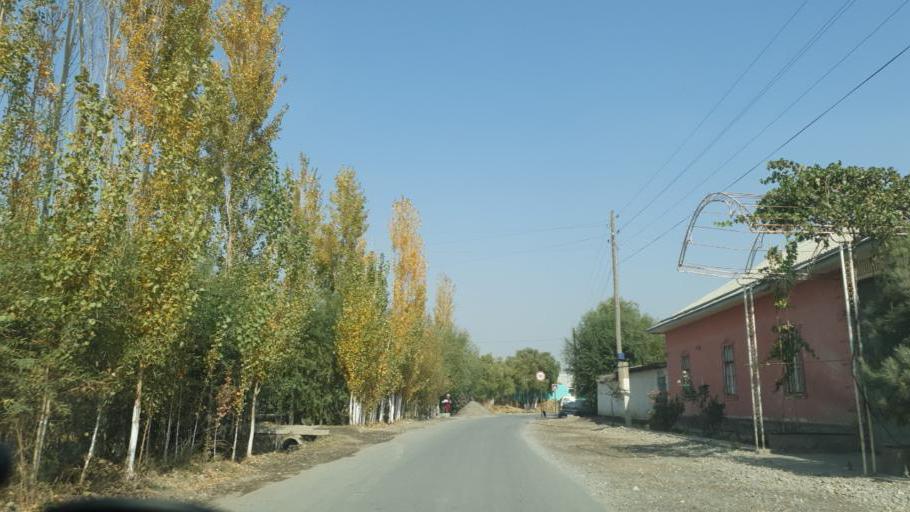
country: UZ
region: Fergana
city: Beshariq
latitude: 40.4941
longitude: 70.6214
